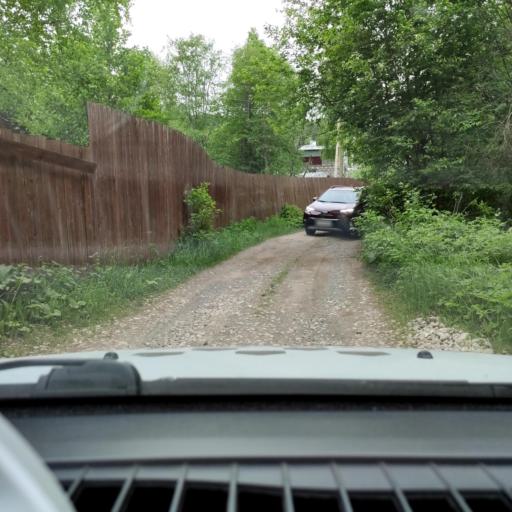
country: RU
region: Perm
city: Novyye Lyady
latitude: 58.0494
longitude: 56.6506
